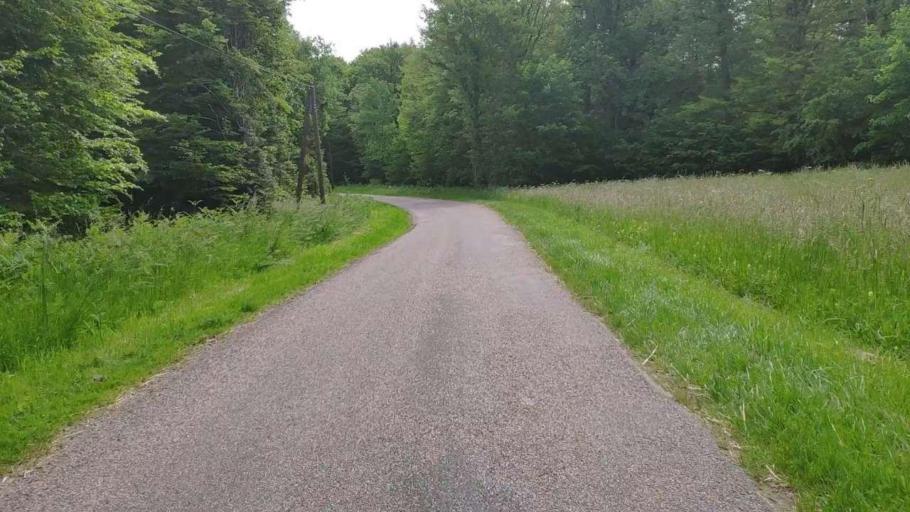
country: FR
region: Franche-Comte
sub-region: Departement du Jura
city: Poligny
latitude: 46.7760
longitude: 5.6396
